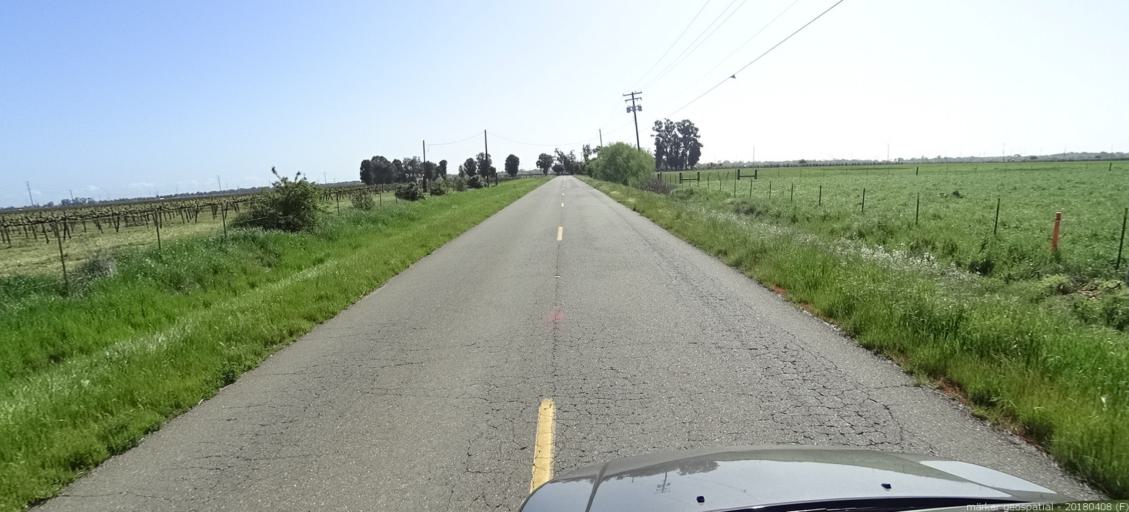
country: US
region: California
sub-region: Sacramento County
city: Elk Grove
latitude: 38.3508
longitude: -121.3746
